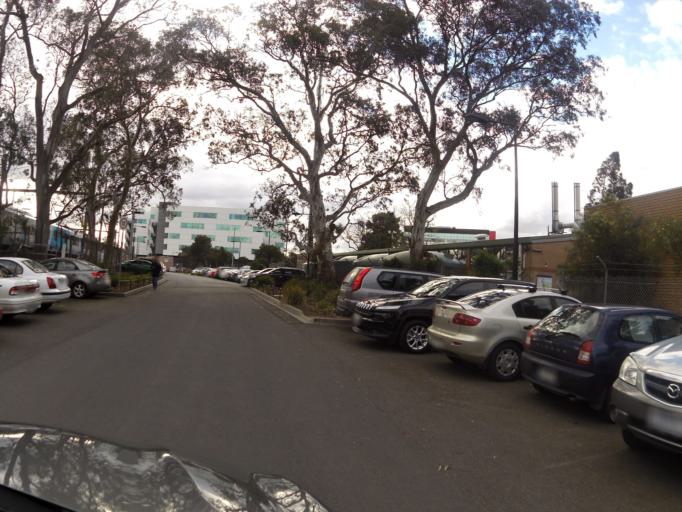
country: AU
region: Victoria
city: Toorak
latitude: -37.8296
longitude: 145.0206
